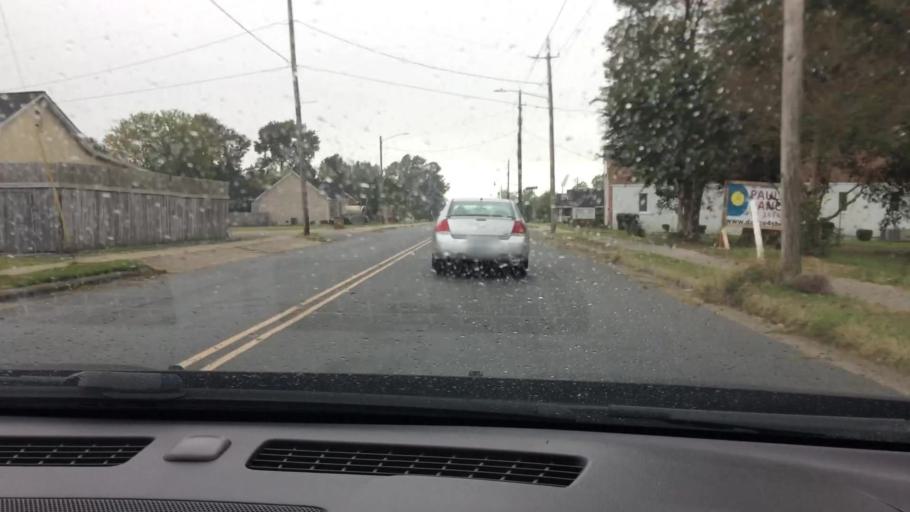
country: US
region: North Carolina
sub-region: Pitt County
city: Greenville
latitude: 35.6130
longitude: -77.3881
